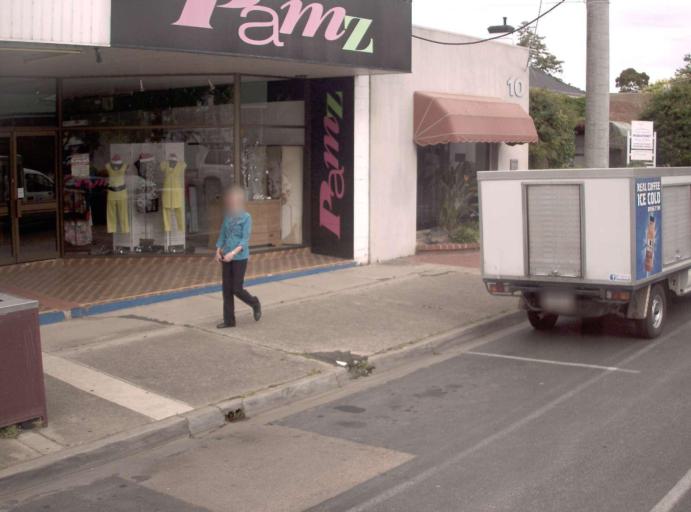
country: AU
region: Victoria
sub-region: East Gippsland
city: Bairnsdale
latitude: -37.8247
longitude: 147.6288
